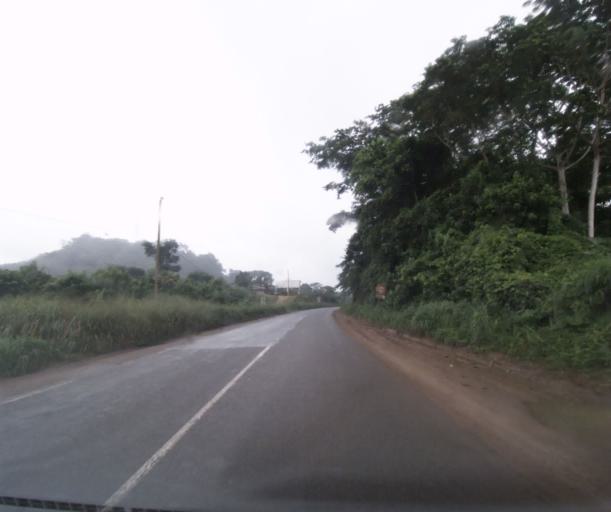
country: CM
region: Centre
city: Eseka
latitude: 3.8871
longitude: 10.7092
